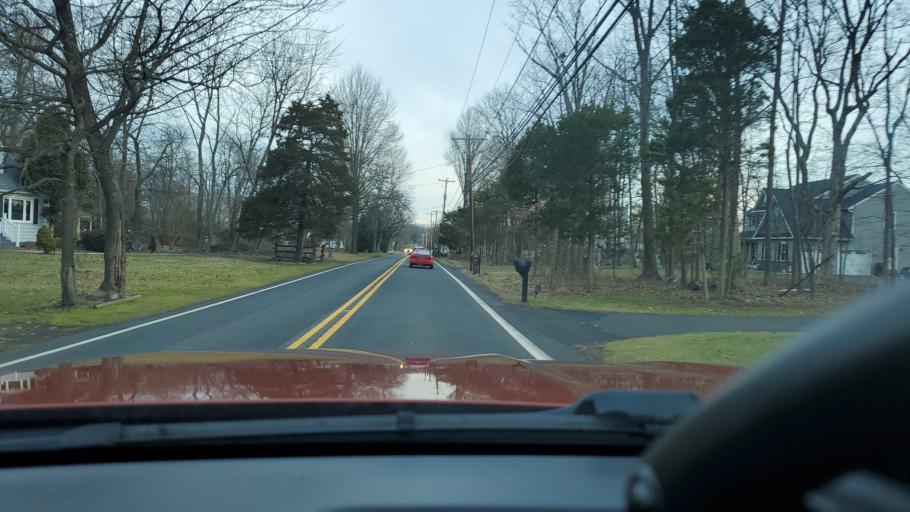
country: US
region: Pennsylvania
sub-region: Montgomery County
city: Woxall
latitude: 40.3408
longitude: -75.4006
